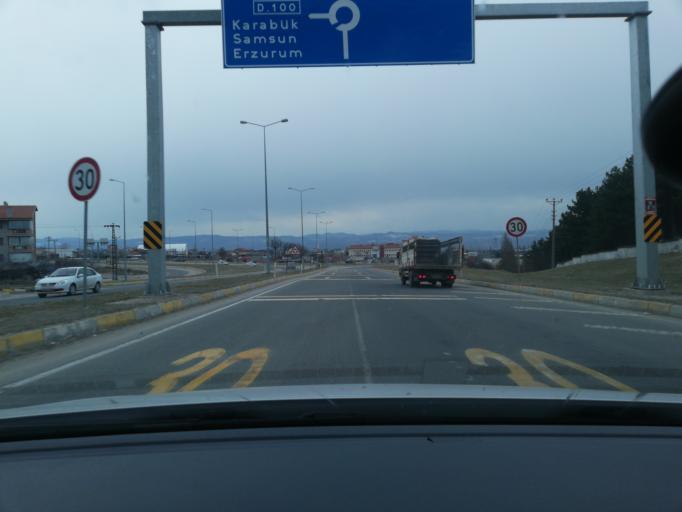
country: TR
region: Bolu
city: Gerede
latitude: 40.7928
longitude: 32.2070
